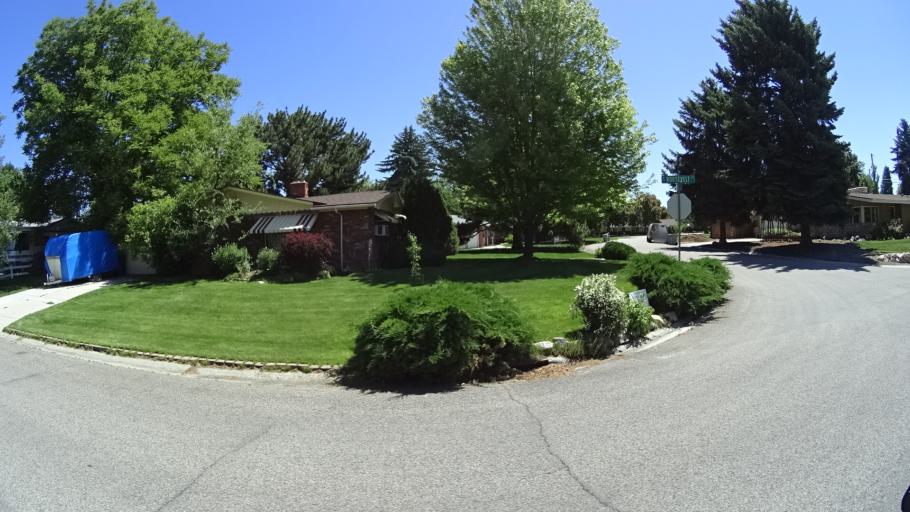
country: US
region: Idaho
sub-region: Ada County
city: Garden City
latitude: 43.5785
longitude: -116.2336
